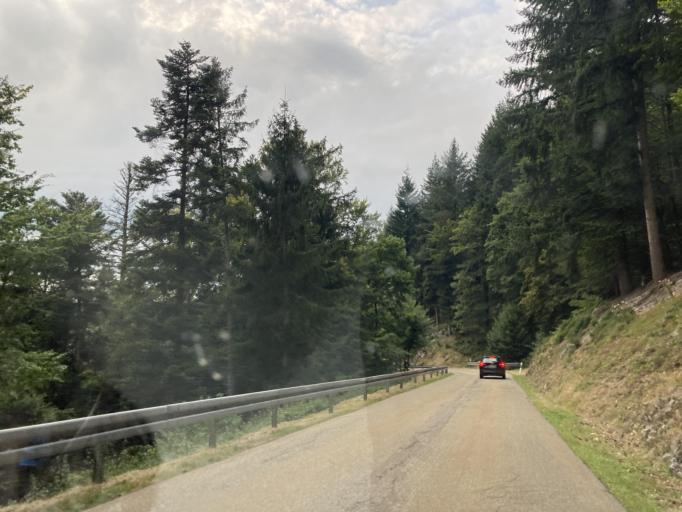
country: DE
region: Baden-Wuerttemberg
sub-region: Freiburg Region
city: Sulzburg
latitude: 47.8021
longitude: 7.7182
